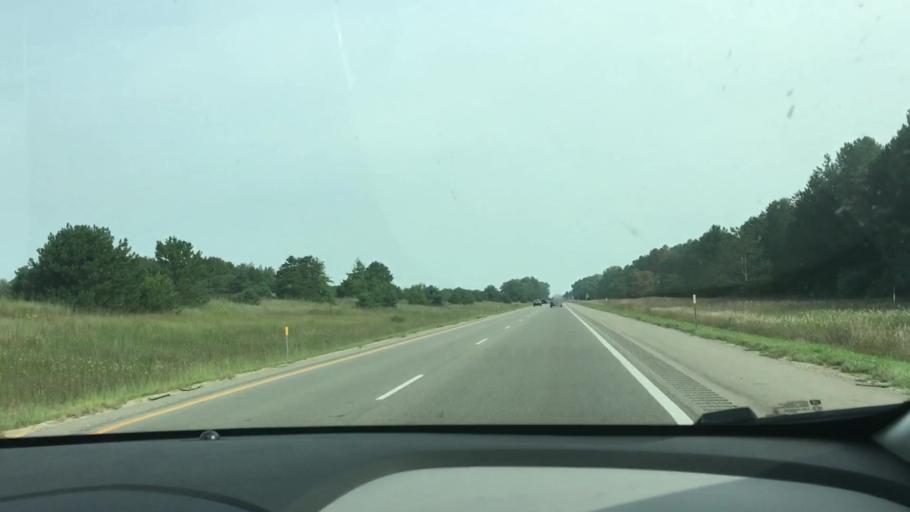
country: US
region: Michigan
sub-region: Kalamazoo County
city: Schoolcraft
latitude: 42.1595
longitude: -85.6440
